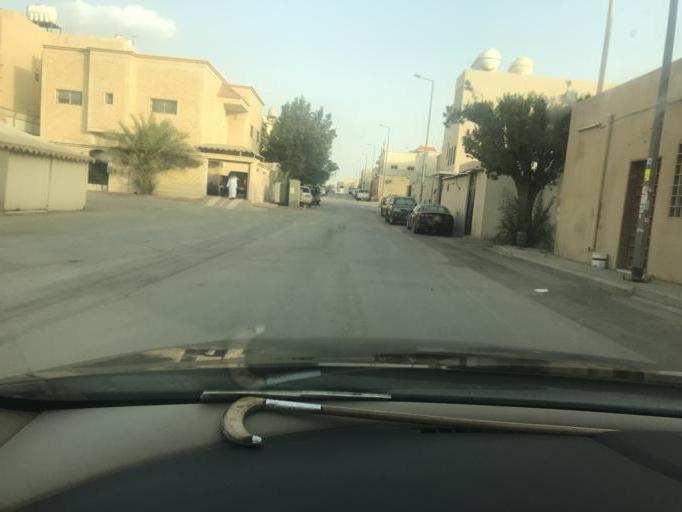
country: SA
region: Ar Riyad
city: Riyadh
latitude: 24.7366
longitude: 46.7764
